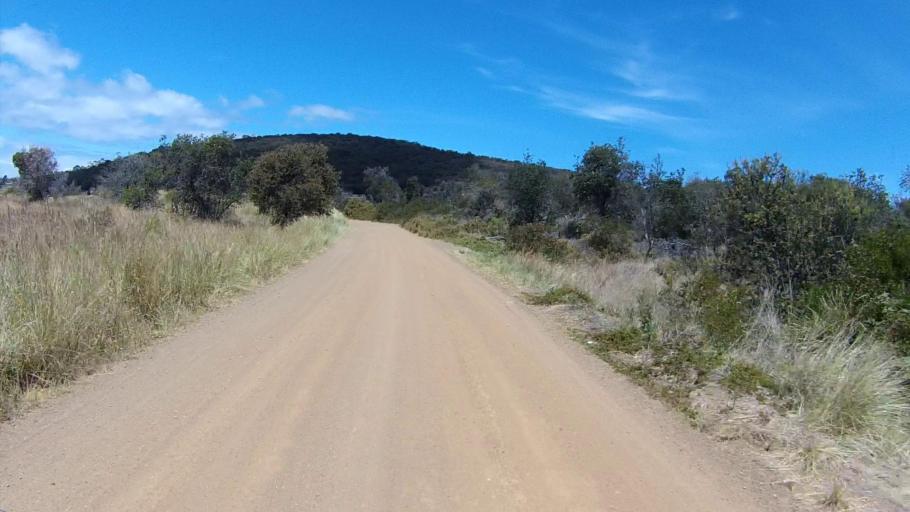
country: AU
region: Tasmania
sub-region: Sorell
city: Sorell
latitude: -42.8751
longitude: 147.6449
